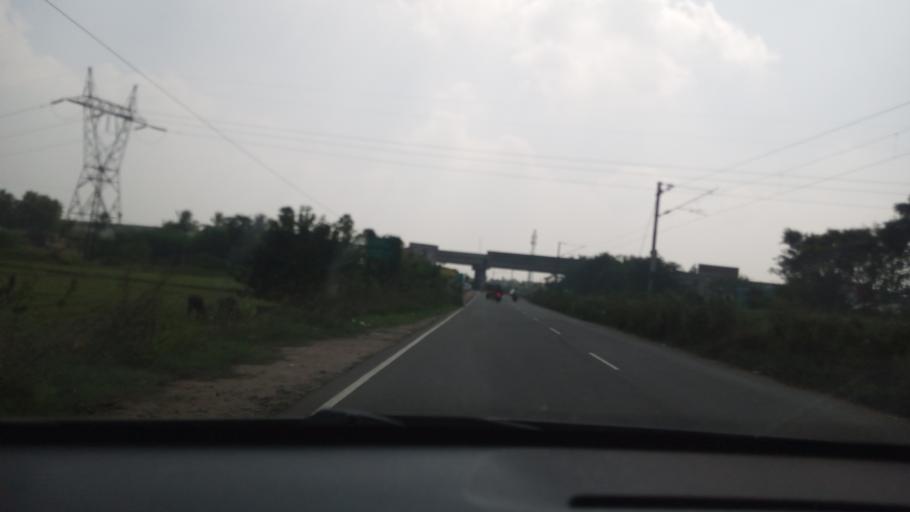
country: IN
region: Tamil Nadu
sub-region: Kancheepuram
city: Kanchipuram
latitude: 12.8761
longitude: 79.6902
